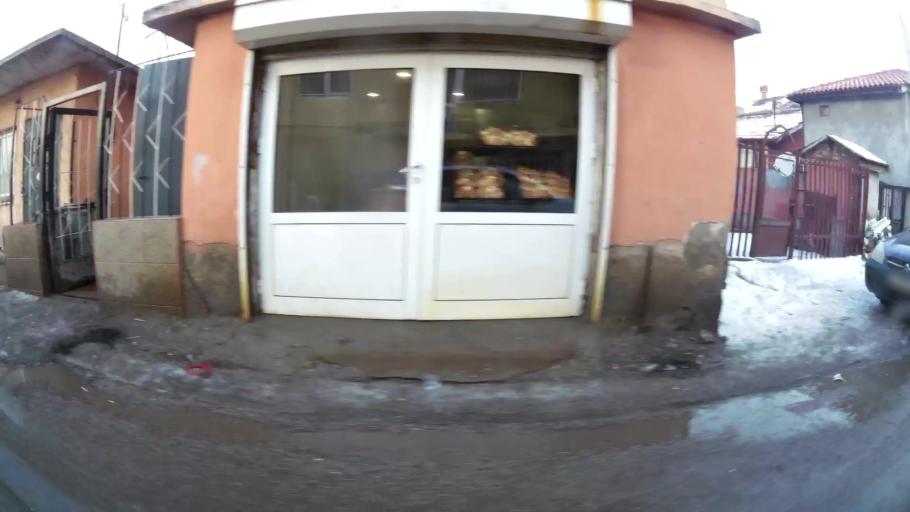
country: BG
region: Sofia-Capital
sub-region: Stolichna Obshtina
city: Sofia
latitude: 42.6954
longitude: 23.2667
